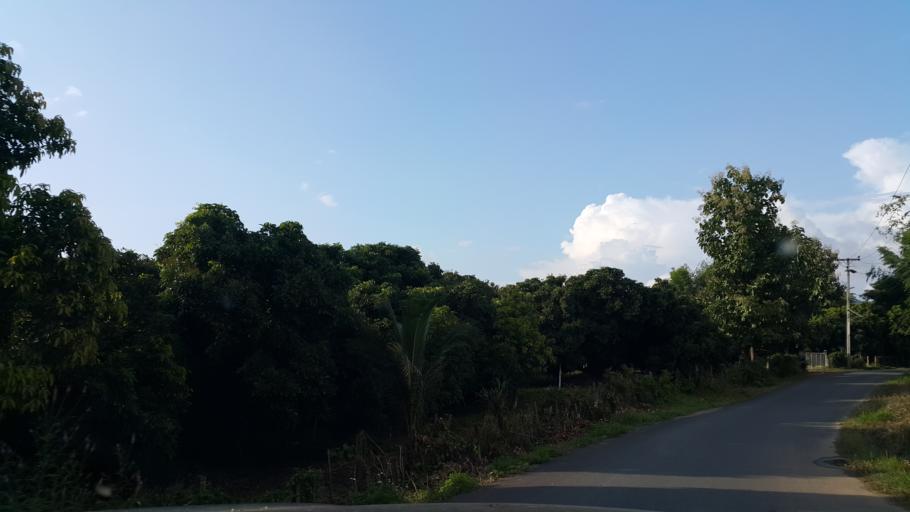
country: TH
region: Chiang Mai
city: Mae On
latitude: 18.7246
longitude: 99.2258
